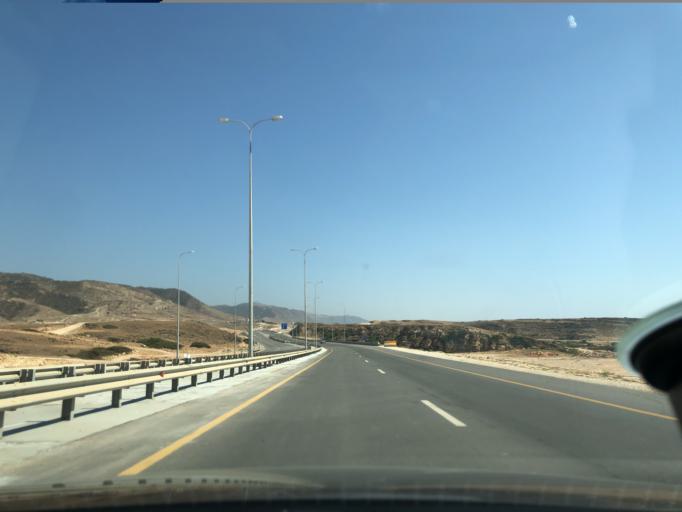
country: OM
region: Zufar
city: Salalah
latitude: 17.0586
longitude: 54.4230
